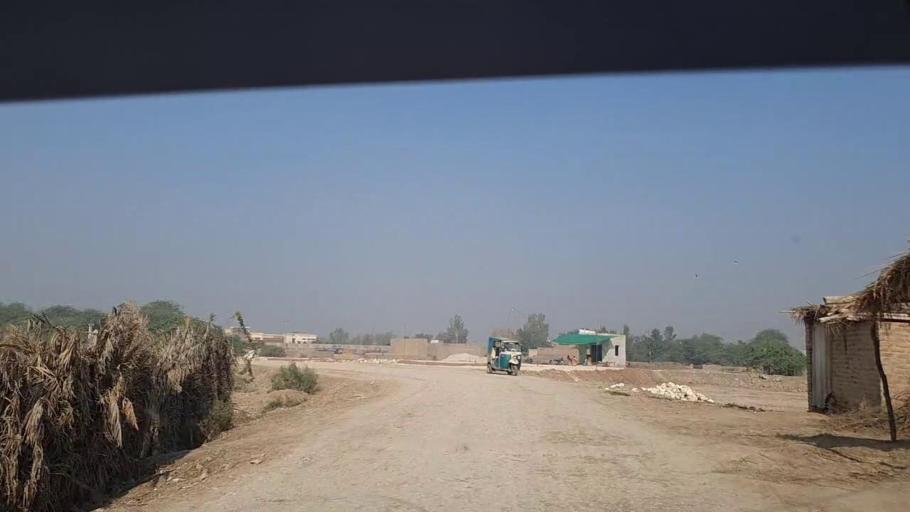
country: PK
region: Sindh
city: Khairpur
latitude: 27.5008
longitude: 68.7361
